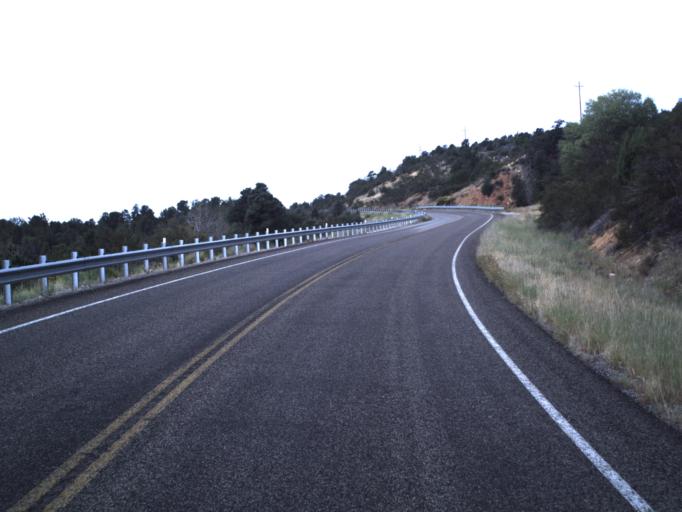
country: US
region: Utah
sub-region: Washington County
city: Hildale
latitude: 37.2537
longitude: -112.7948
